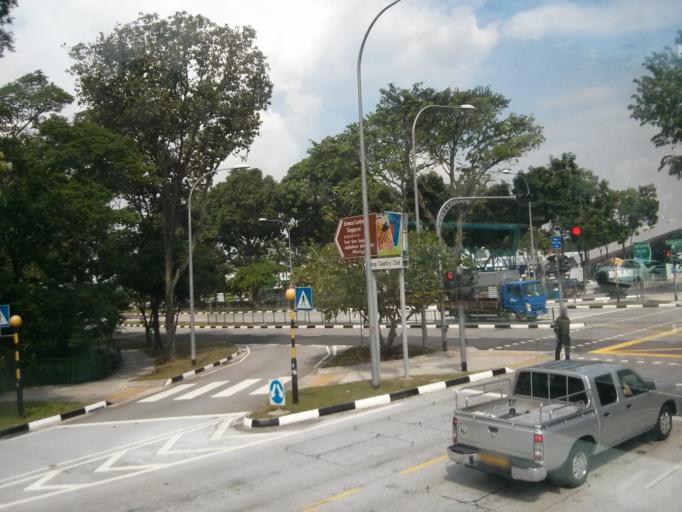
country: SG
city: Singapore
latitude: 1.3330
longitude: 103.7379
